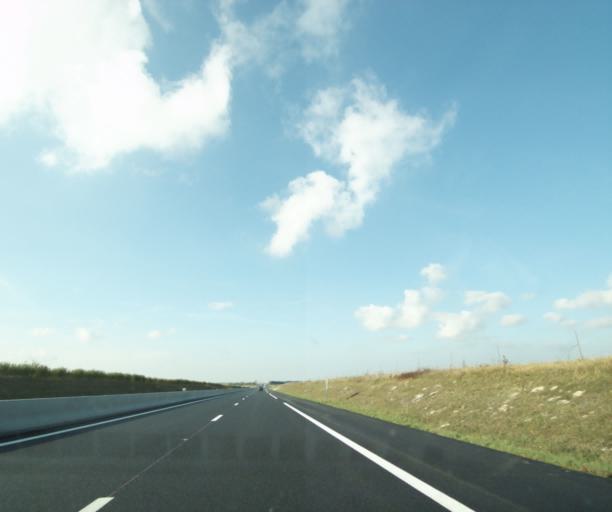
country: FR
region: Champagne-Ardenne
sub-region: Departement de la Marne
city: Courtisols
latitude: 49.0357
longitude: 4.6041
